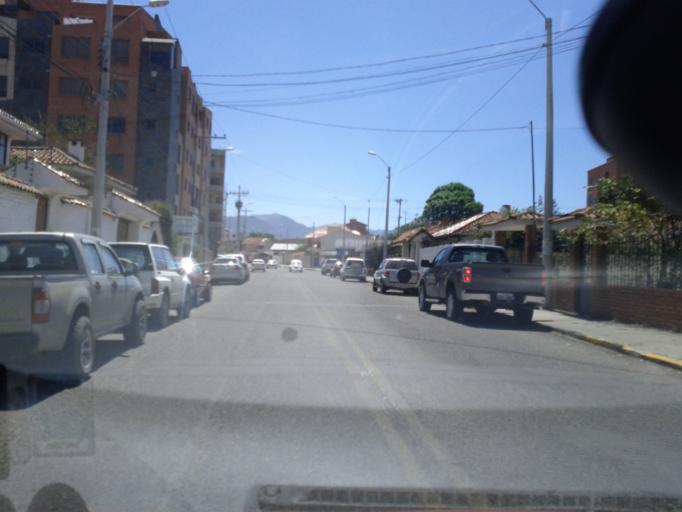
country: EC
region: Azuay
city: Cuenca
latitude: -2.9088
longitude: -79.0110
